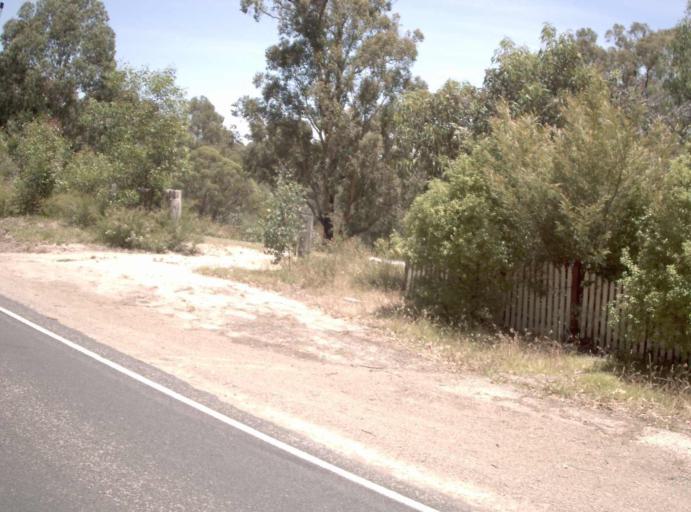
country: AU
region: Victoria
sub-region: East Gippsland
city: Lakes Entrance
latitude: -37.6884
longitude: 147.8400
